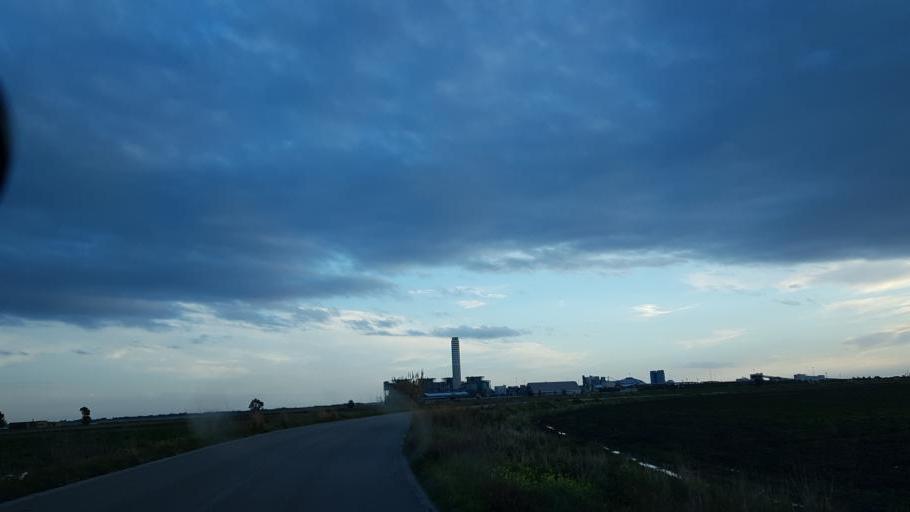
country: IT
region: Apulia
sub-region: Provincia di Brindisi
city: La Rosa
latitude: 40.5834
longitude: 18.0334
